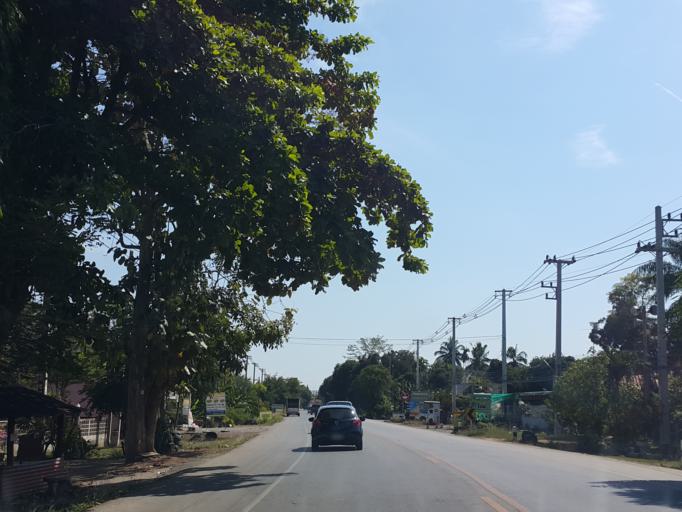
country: TH
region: Sukhothai
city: Sawankhalok
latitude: 17.2910
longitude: 99.8390
